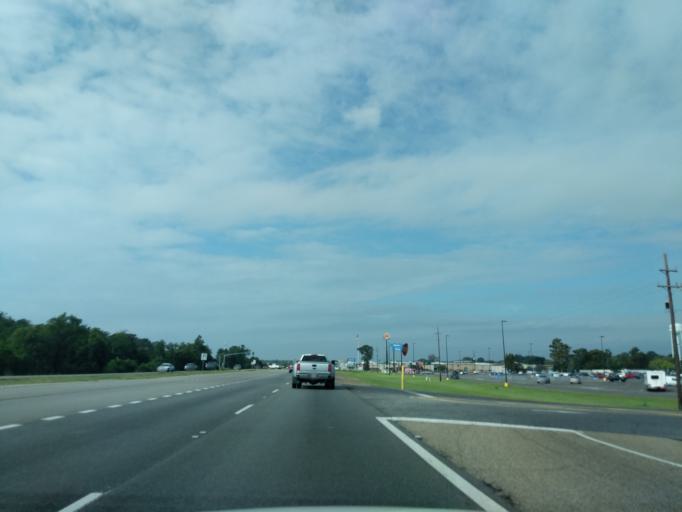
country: US
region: Louisiana
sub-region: Saint Mary Parish
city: Bayou Vista
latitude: 29.6821
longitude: -91.2650
